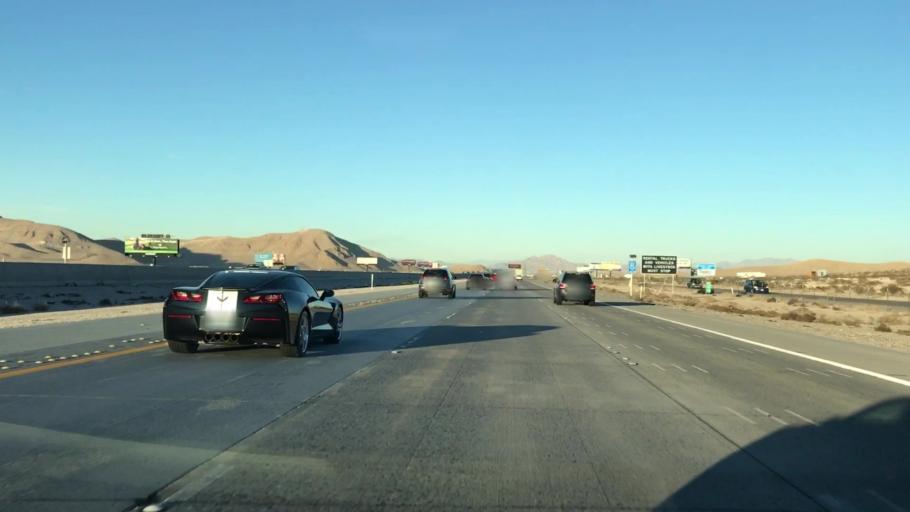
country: US
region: Nevada
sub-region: Clark County
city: Enterprise
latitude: 35.9100
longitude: -115.2063
